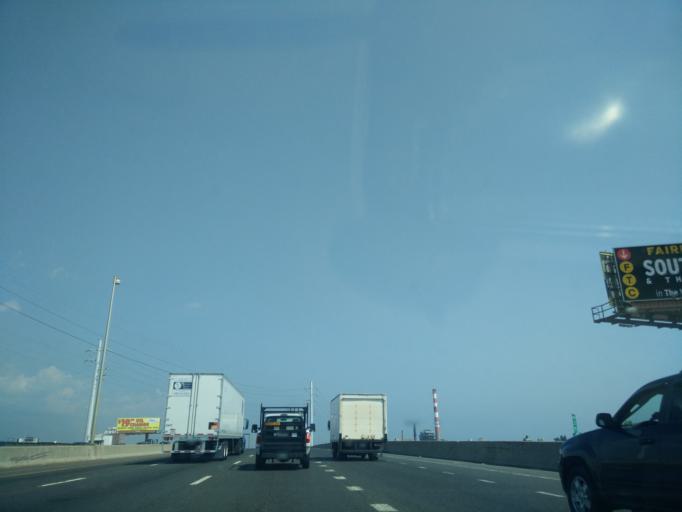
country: US
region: Connecticut
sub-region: Fairfield County
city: Bridgeport
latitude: 41.1681
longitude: -73.1998
